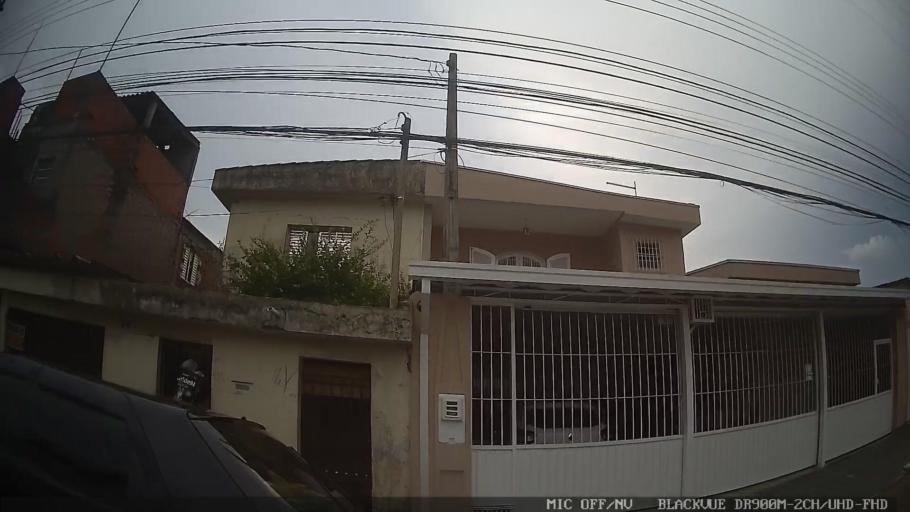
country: BR
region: Sao Paulo
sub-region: Suzano
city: Suzano
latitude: -23.5439
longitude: -46.2968
